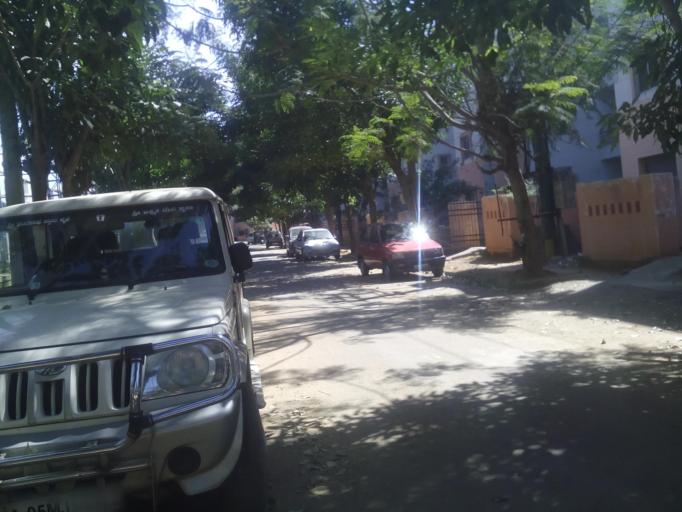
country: IN
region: Karnataka
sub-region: Bangalore Urban
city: Anekal
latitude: 12.7891
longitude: 77.7019
